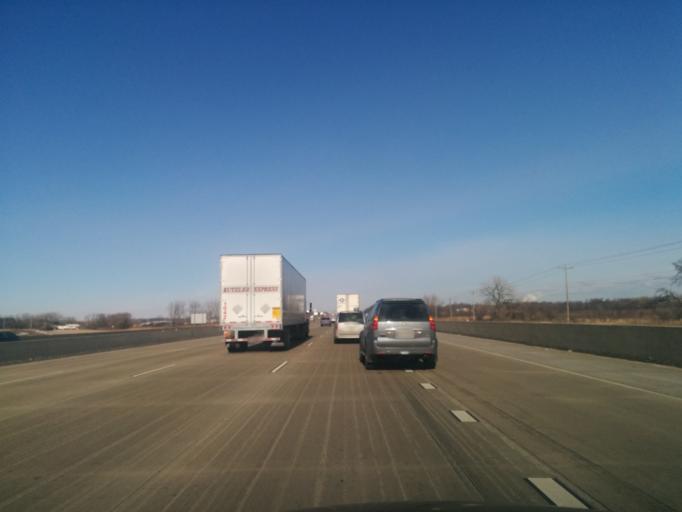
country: US
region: Wisconsin
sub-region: Kenosha County
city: Pleasant Prairie
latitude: 42.5338
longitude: -87.9520
